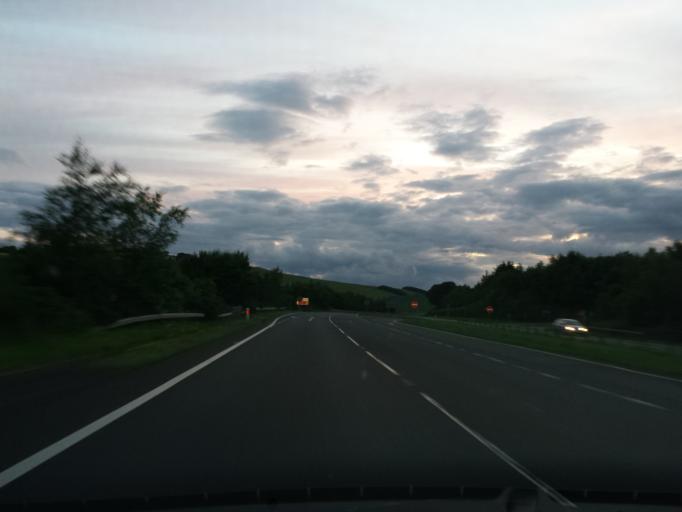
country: GB
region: Scotland
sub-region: The Scottish Borders
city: Chirnside
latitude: 55.8568
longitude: -2.2290
